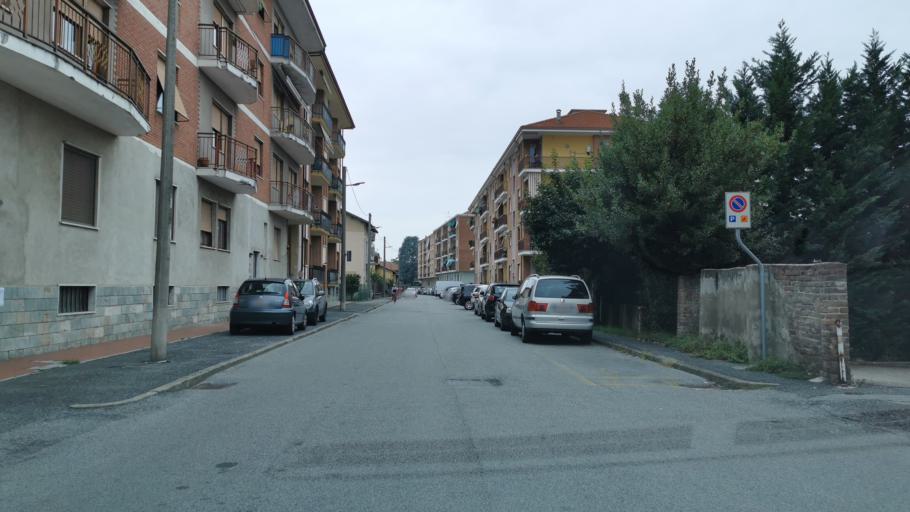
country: IT
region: Piedmont
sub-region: Provincia di Cuneo
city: Bra
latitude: 44.6923
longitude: 7.8583
